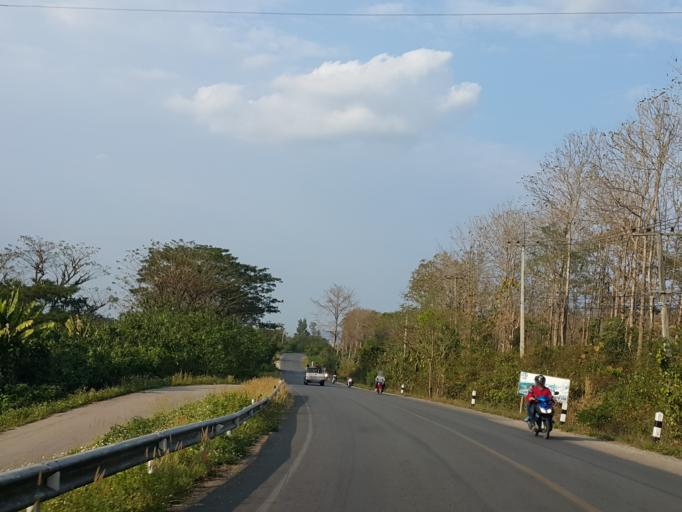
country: TH
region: Lampang
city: Lampang
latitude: 18.4640
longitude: 99.4606
